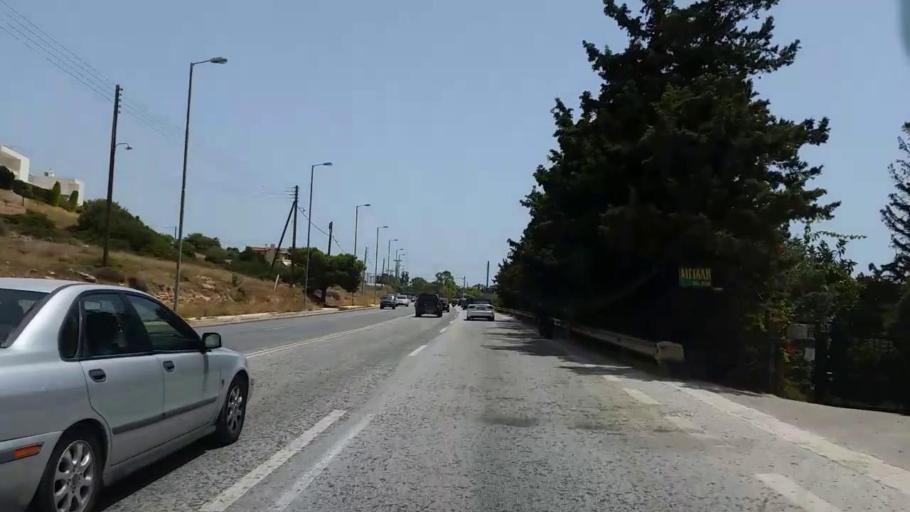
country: GR
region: Attica
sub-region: Nomarchia Anatolikis Attikis
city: Agia Marina
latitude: 37.8100
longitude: 23.8464
